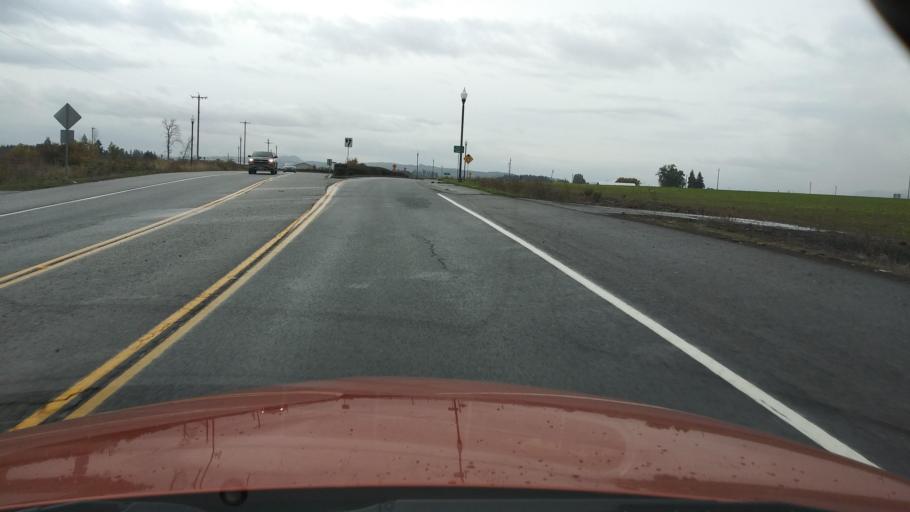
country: US
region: Oregon
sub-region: Washington County
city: Cornelius
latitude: 45.5534
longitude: -123.0641
